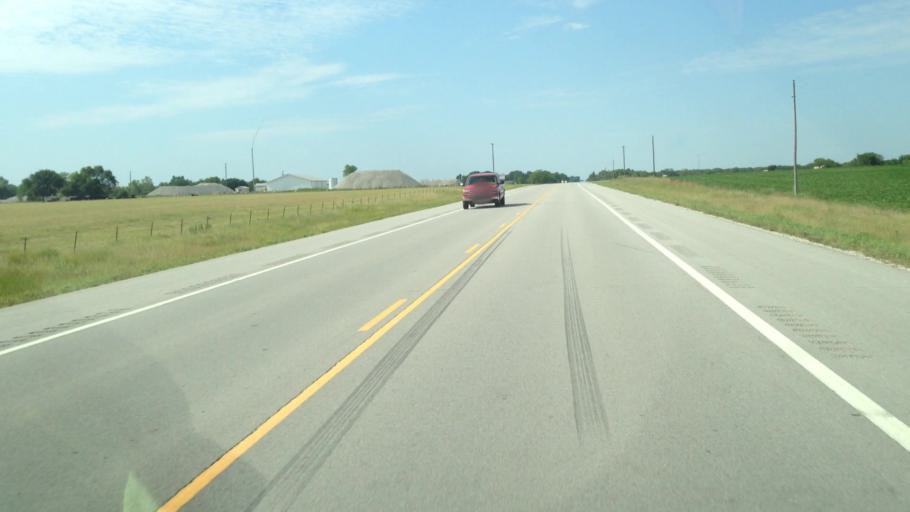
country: US
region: Kansas
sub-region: Labette County
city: Parsons
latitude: 37.2787
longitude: -95.2674
